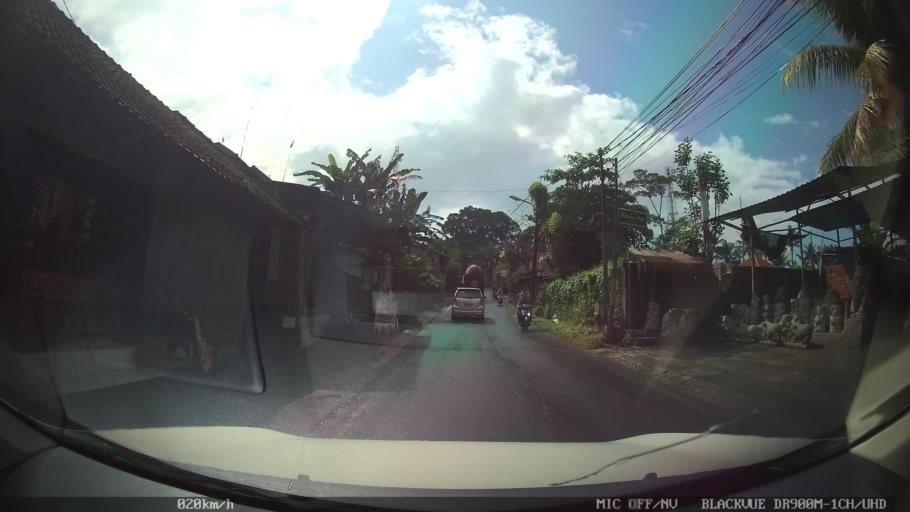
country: ID
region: Bali
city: Banjar Tebongkang
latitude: -8.5416
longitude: 115.2656
